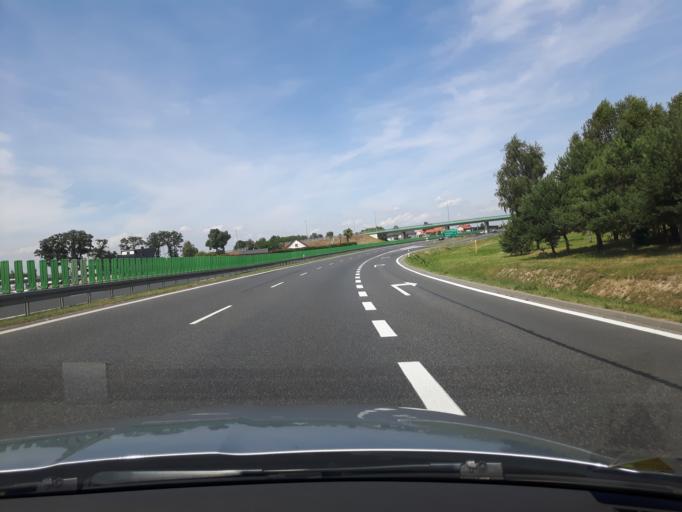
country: PL
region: Masovian Voivodeship
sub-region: Powiat plonski
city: Zaluski
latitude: 52.5089
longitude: 20.5298
